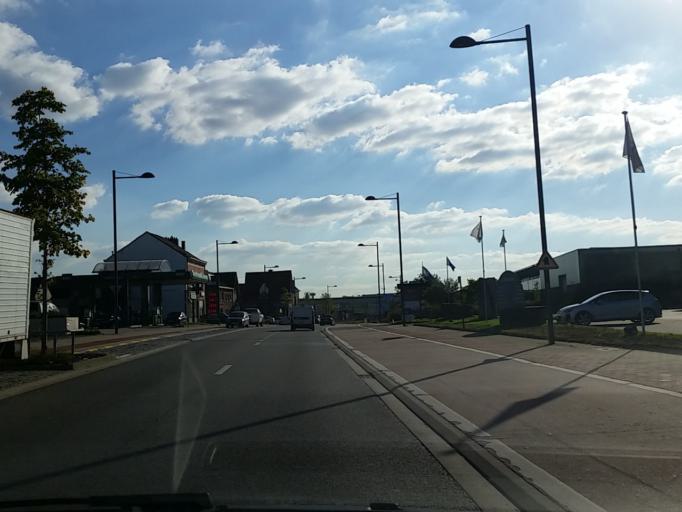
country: BE
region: Flanders
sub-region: Provincie Vlaams-Brabant
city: Diegem
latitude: 50.8861
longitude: 4.4229
